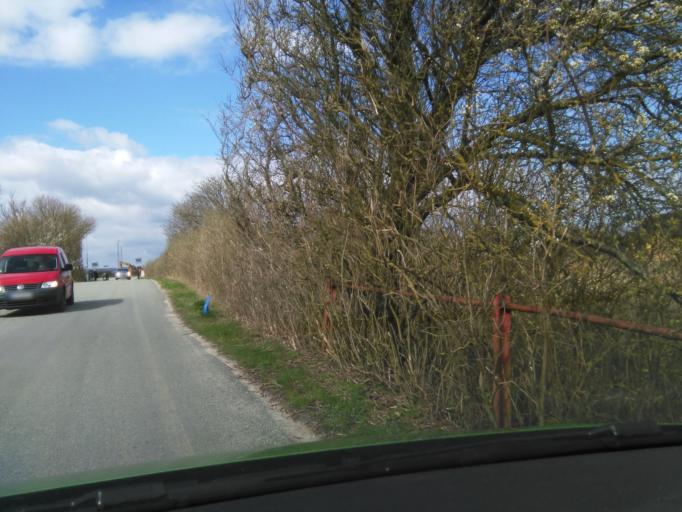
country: DK
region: South Denmark
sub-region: Middelfart Kommune
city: Brenderup
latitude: 55.5164
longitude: 9.9545
